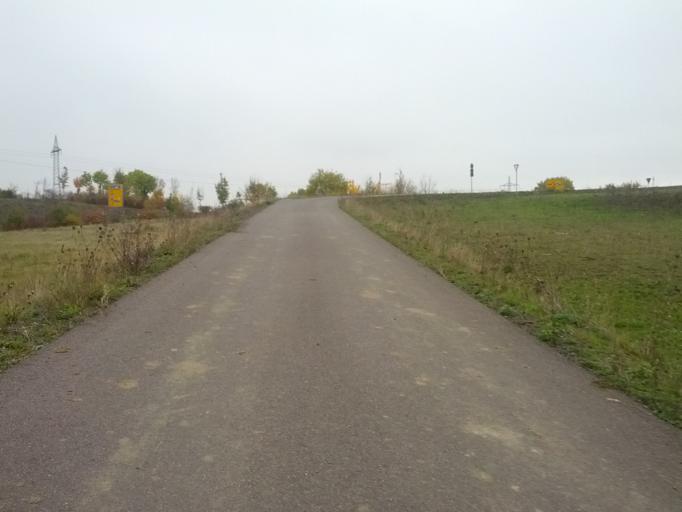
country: DE
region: Thuringia
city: Thal
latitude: 50.9673
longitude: 10.3793
